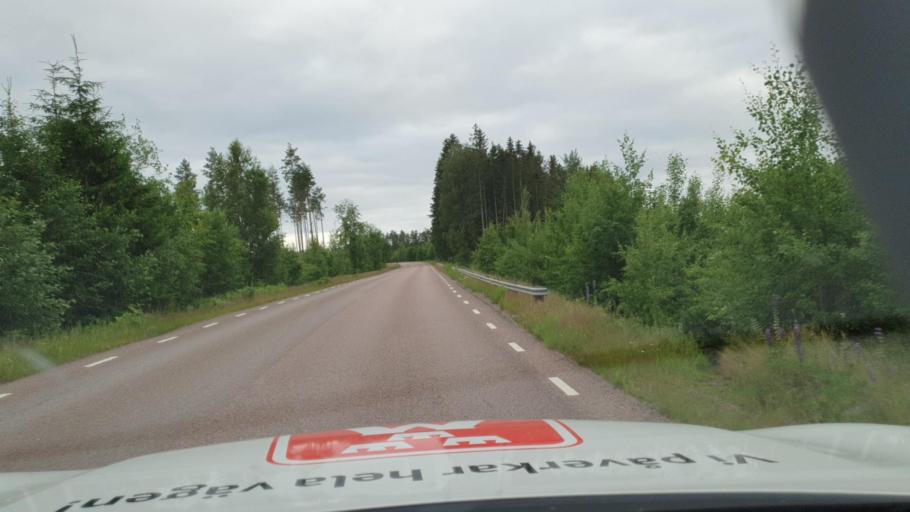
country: SE
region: Vaermland
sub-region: Forshaga Kommun
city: Forshaga
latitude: 59.4971
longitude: 13.4026
